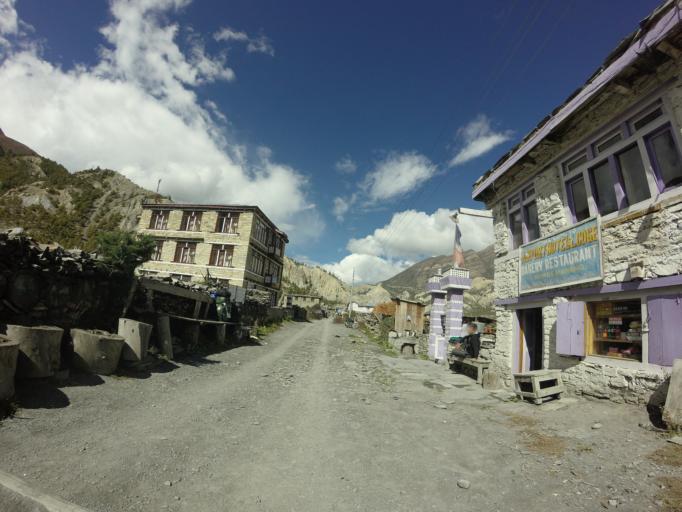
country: NP
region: Western Region
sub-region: Gandaki Zone
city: Nawal
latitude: 28.6376
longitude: 84.0915
